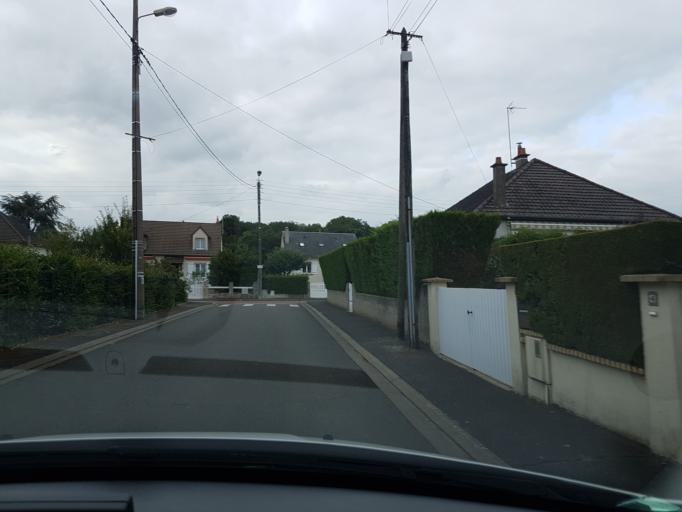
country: FR
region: Centre
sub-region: Departement d'Indre-et-Loire
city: Saint-Avertin
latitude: 47.3658
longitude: 0.7499
